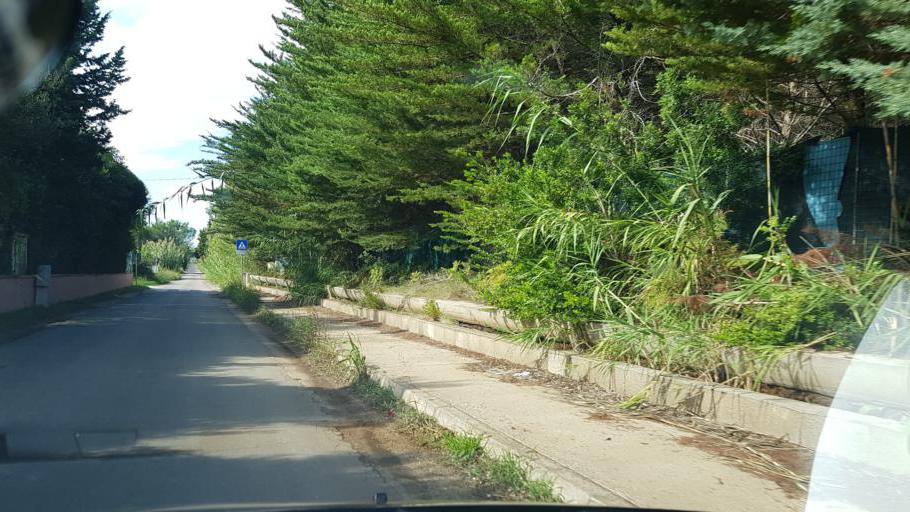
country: IT
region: Apulia
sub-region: Provincia di Lecce
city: Borgagne
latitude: 40.2301
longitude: 18.4501
